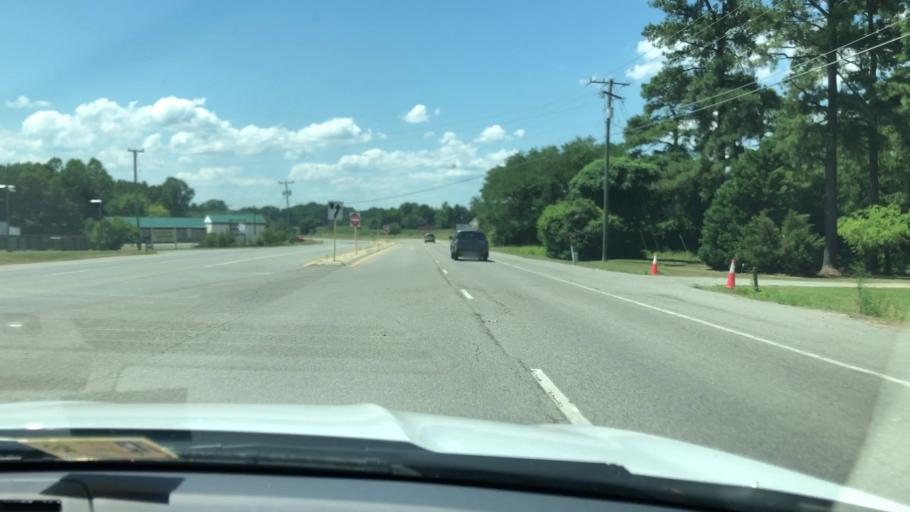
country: US
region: Virginia
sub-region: Middlesex County
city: Saluda
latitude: 37.5996
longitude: -76.5127
